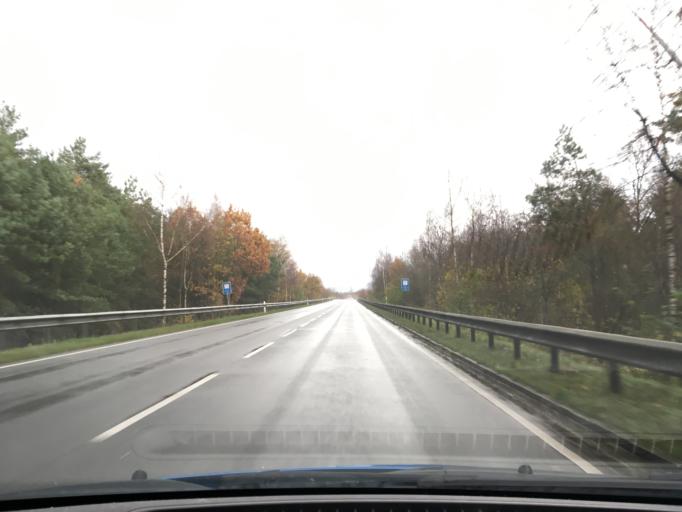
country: DE
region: Lower Saxony
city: Embsen
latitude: 53.1945
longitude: 10.3750
